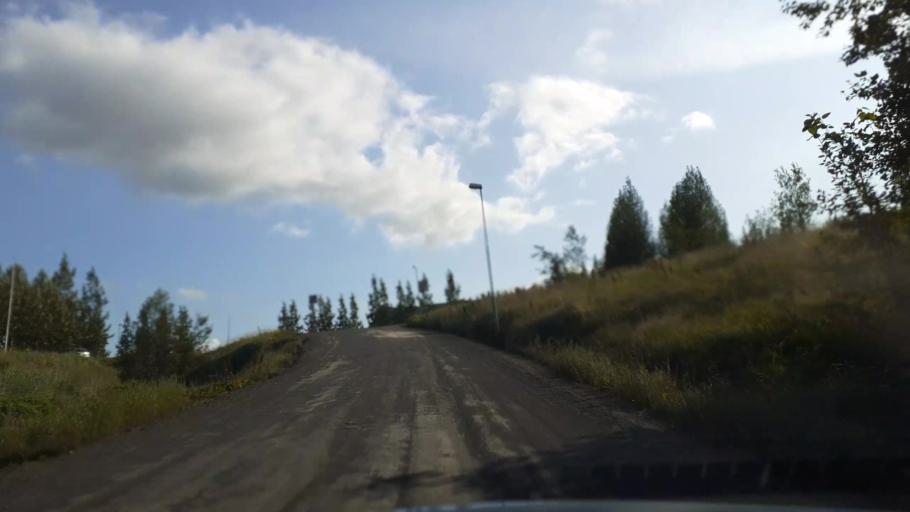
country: IS
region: Northeast
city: Akureyri
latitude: 65.6686
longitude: -18.0943
